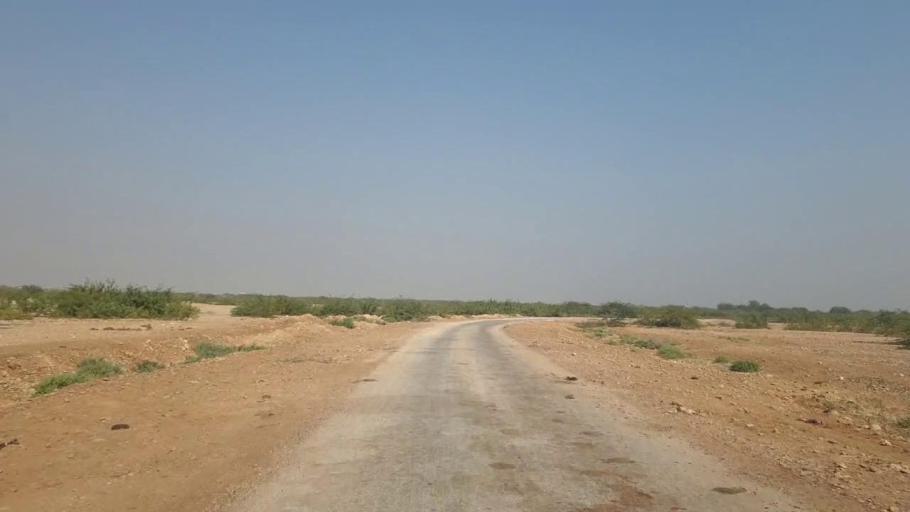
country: PK
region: Sindh
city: Jamshoro
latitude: 25.5388
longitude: 68.3451
